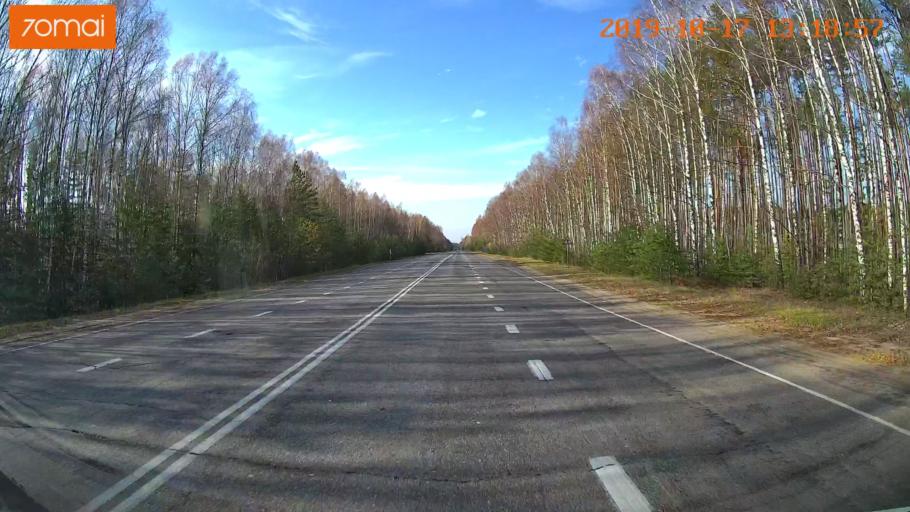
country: RU
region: Rjazan
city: Gus'-Zheleznyy
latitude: 55.0663
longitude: 41.0856
